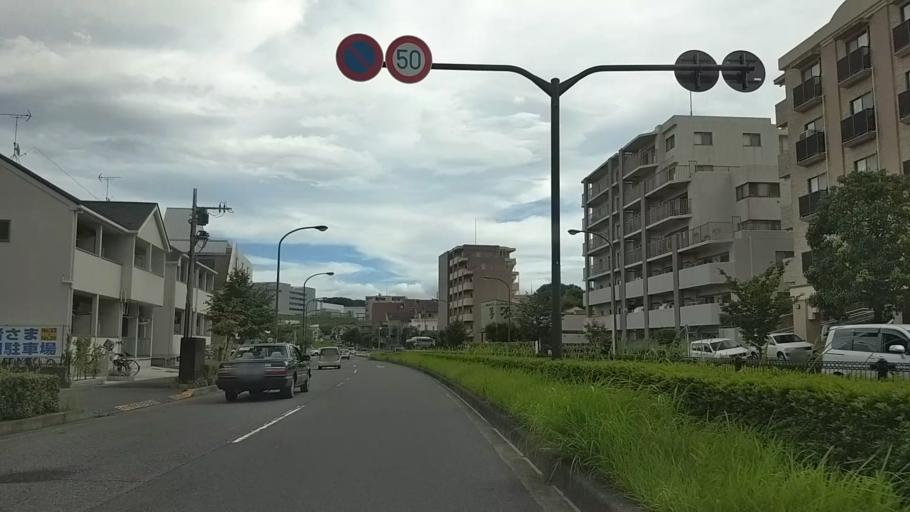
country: JP
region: Tokyo
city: Hachioji
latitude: 35.6275
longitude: 139.3272
